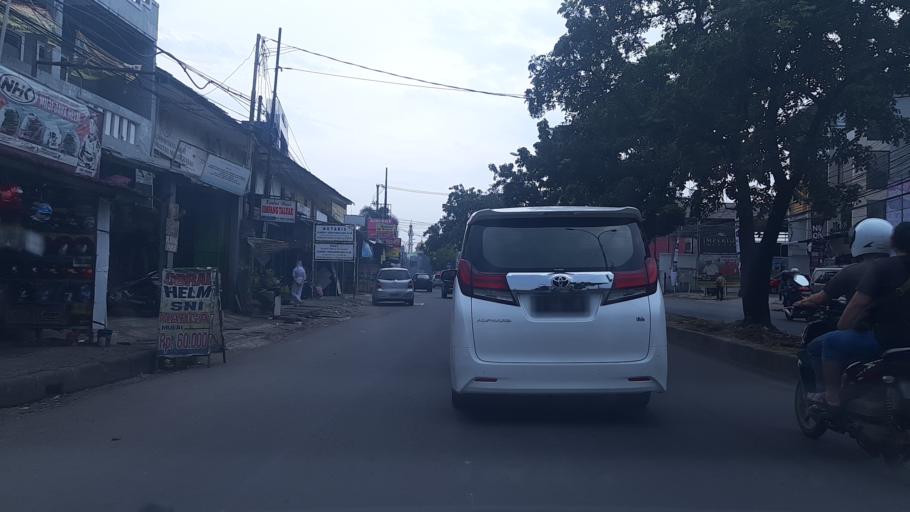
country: ID
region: West Java
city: Cibinong
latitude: -6.4748
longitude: 106.8634
